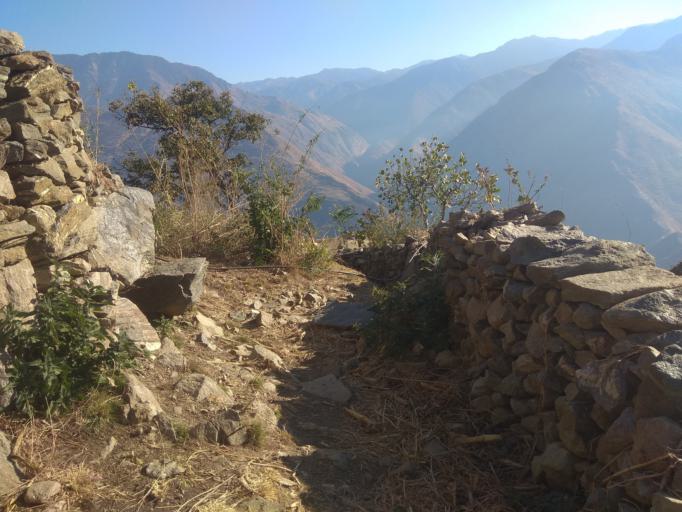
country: NP
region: Mid Western
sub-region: Karnali Zone
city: Jumla
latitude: 29.3137
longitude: 81.7394
